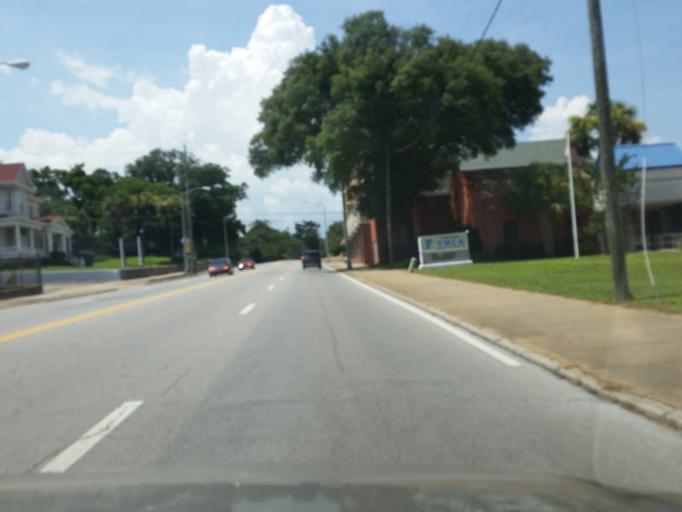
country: US
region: Florida
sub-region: Escambia County
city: Pensacola
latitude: 30.4177
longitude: -87.2165
